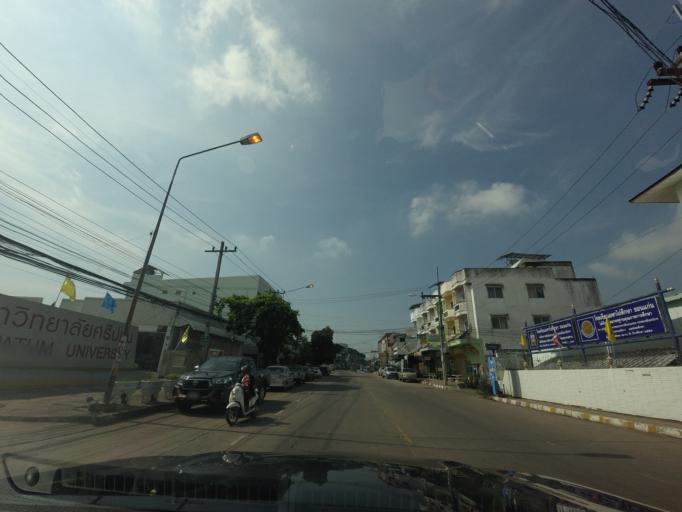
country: TH
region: Khon Kaen
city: Khon Kaen
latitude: 16.4270
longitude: 102.8512
